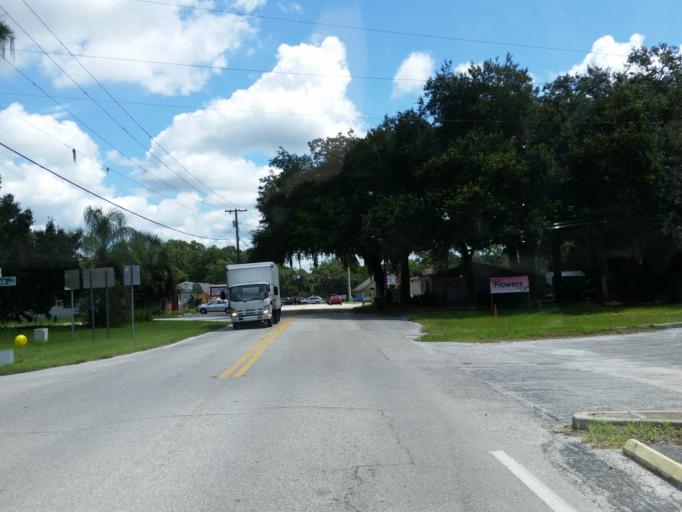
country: US
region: Florida
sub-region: Hillsborough County
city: Riverview
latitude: 27.8717
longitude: -82.3284
